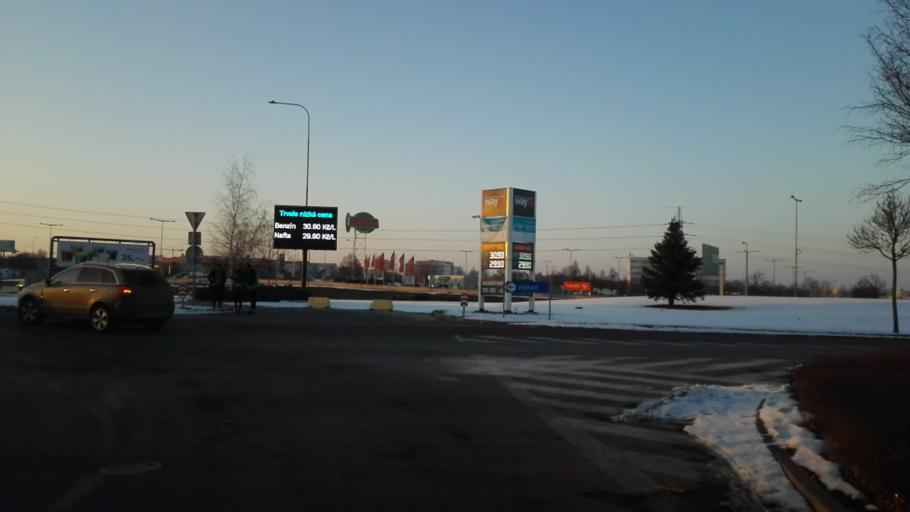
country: CZ
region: Central Bohemia
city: Hostivice
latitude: 50.0510
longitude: 14.2957
